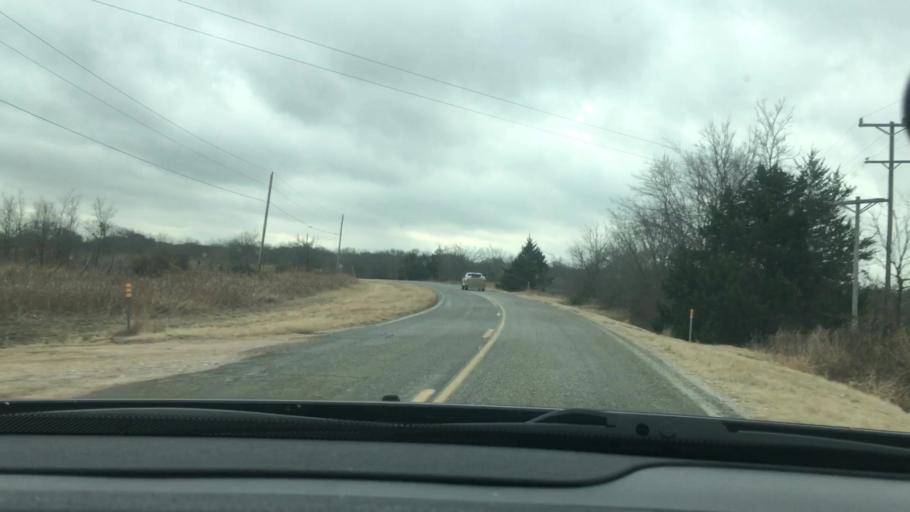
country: US
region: Oklahoma
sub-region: Johnston County
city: Tishomingo
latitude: 34.1447
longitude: -96.5490
